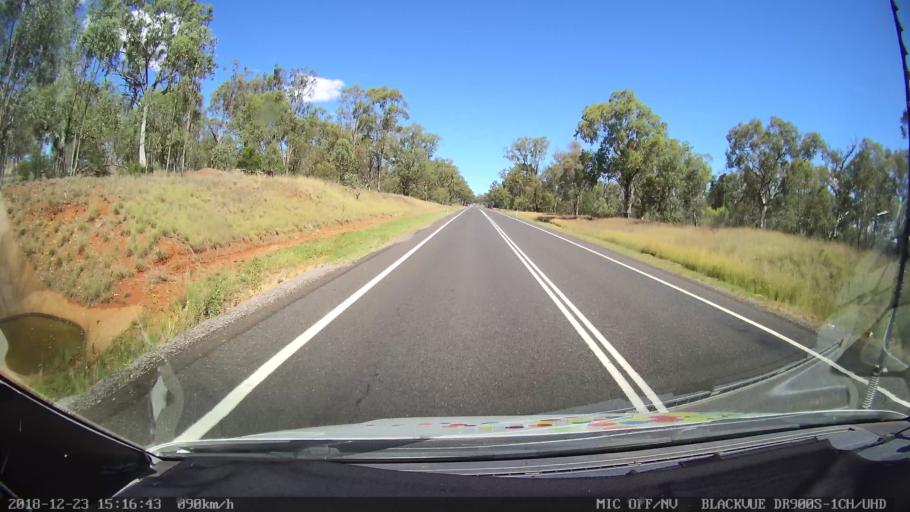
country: AU
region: New South Wales
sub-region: Tamworth Municipality
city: Manilla
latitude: -30.8019
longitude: 150.7504
